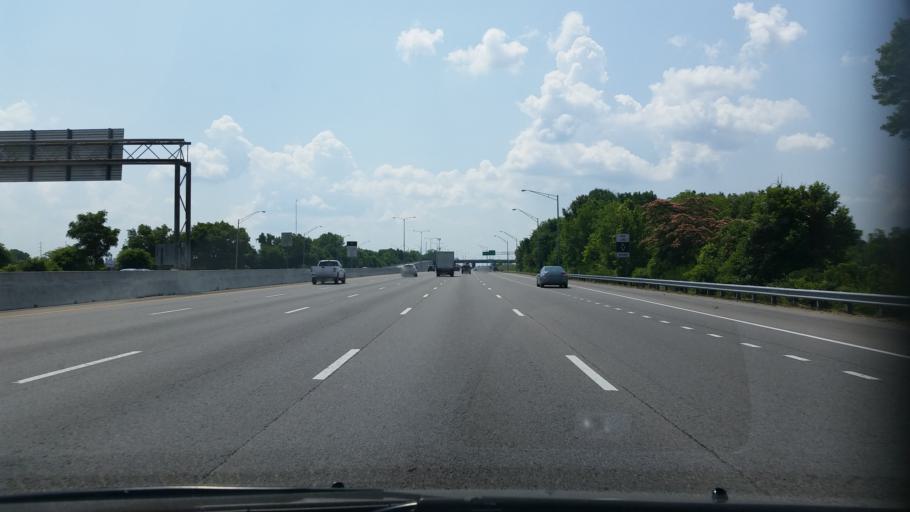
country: US
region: Tennessee
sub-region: Davidson County
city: Oak Hill
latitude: 36.1071
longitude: -86.7686
